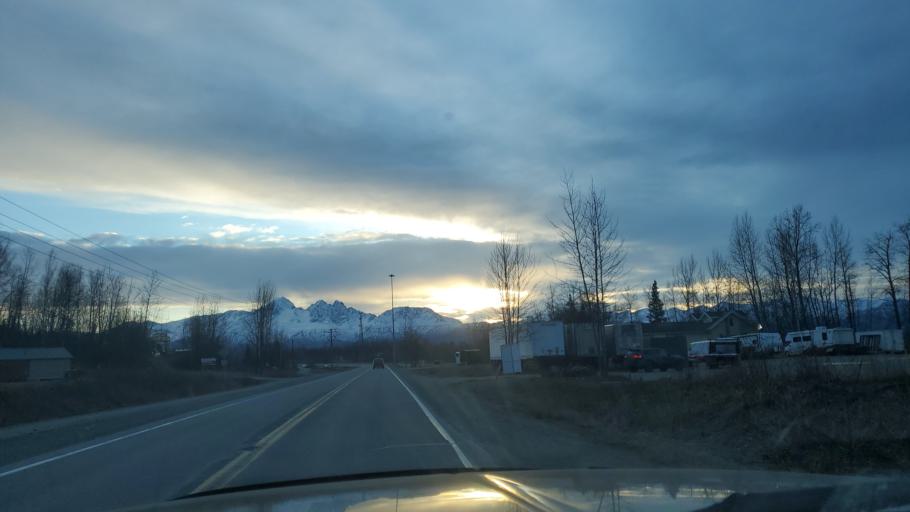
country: US
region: Alaska
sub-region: Matanuska-Susitna Borough
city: Lakes
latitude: 61.5686
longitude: -149.3098
